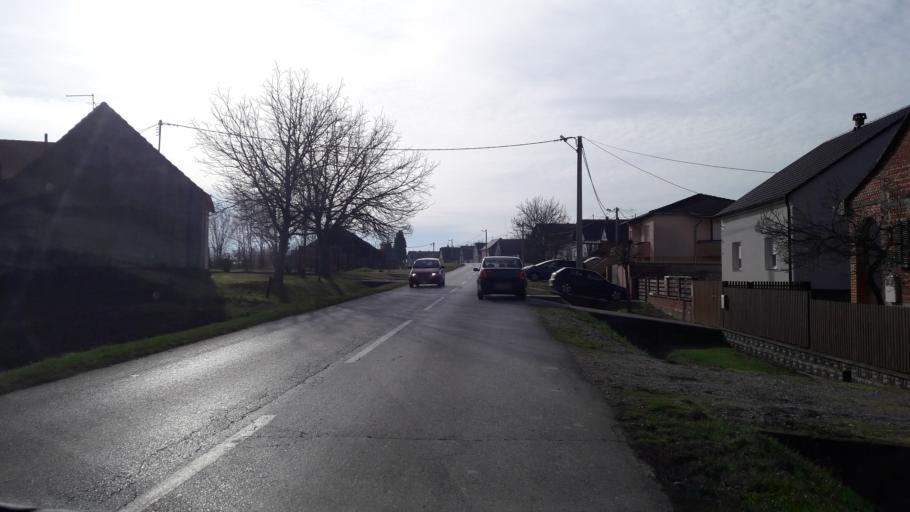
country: HR
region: Vukovarsko-Srijemska
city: Vodinci
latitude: 45.2929
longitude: 18.5595
